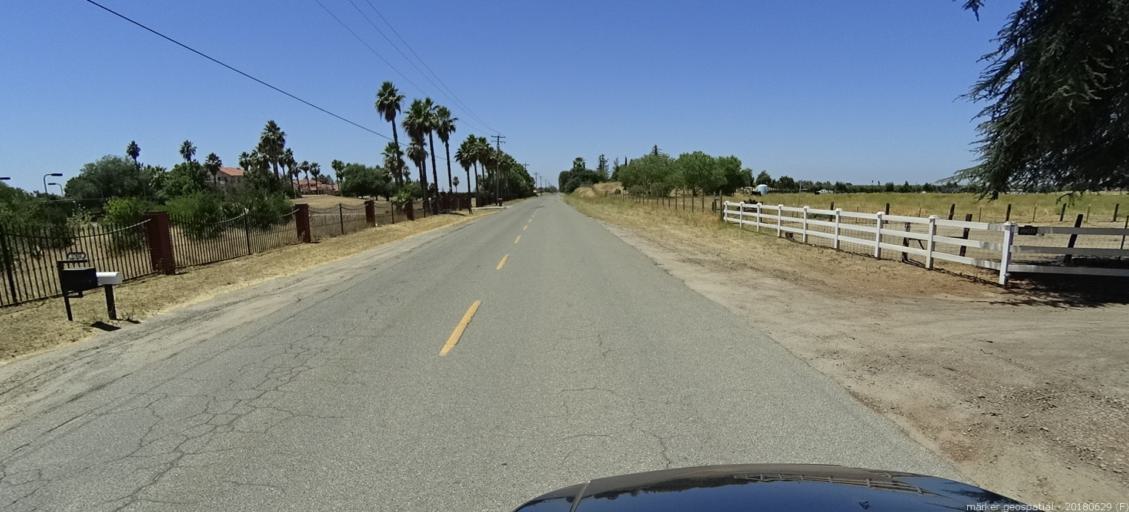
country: US
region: California
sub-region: Madera County
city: Parksdale
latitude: 36.9994
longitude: -119.9910
